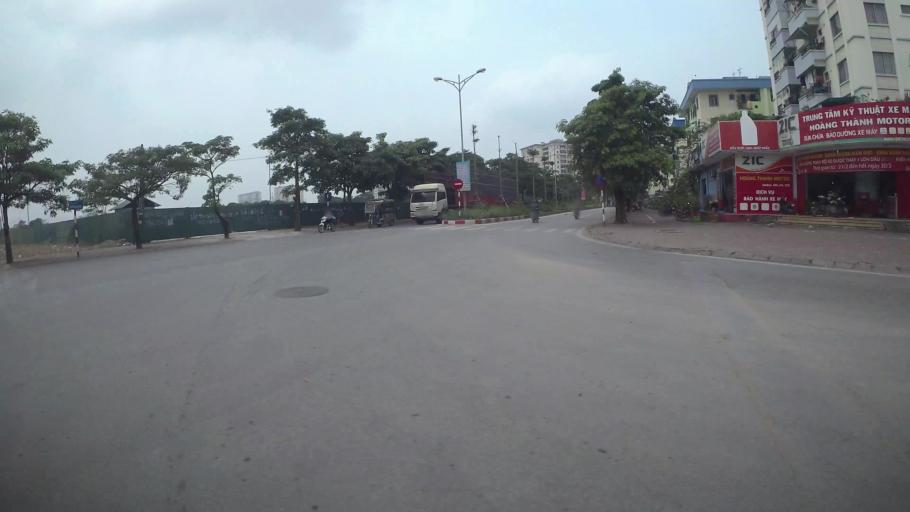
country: VN
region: Ha Noi
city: Trau Quy
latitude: 21.0615
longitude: 105.9077
